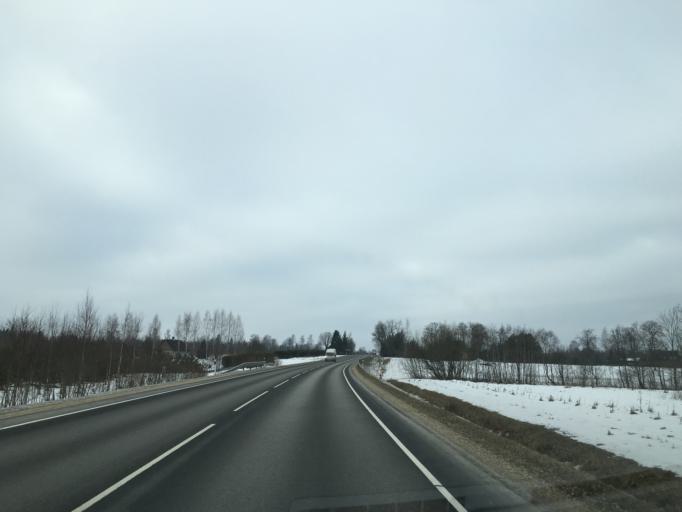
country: EE
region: Tartu
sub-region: Elva linn
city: Elva
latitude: 58.1723
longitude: 26.3307
